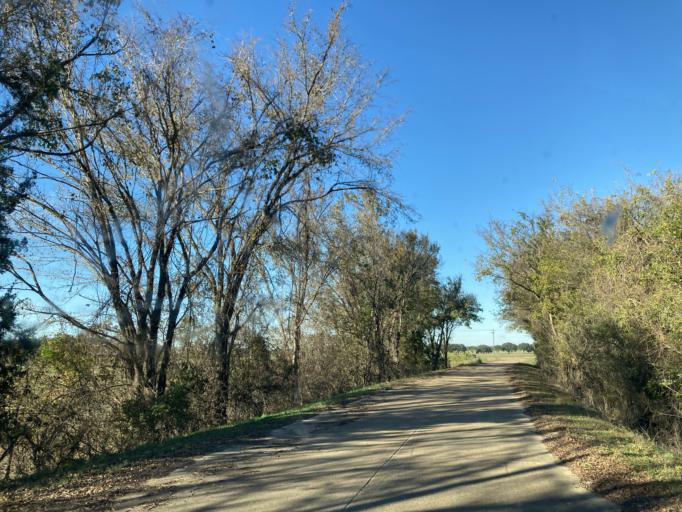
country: US
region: Mississippi
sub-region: Yazoo County
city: Yazoo City
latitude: 32.7512
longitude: -90.4872
